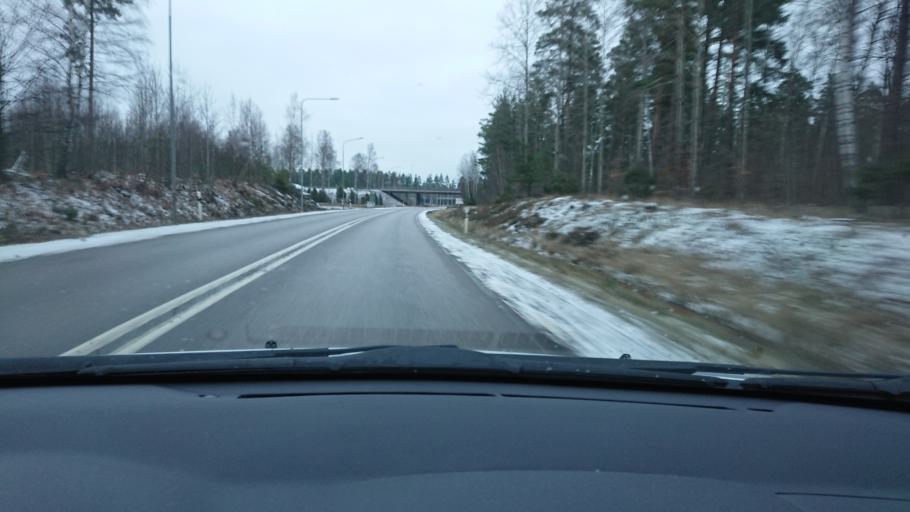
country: SE
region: Kalmar
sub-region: Hultsfreds Kommun
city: Hultsfred
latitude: 57.4986
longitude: 15.8210
